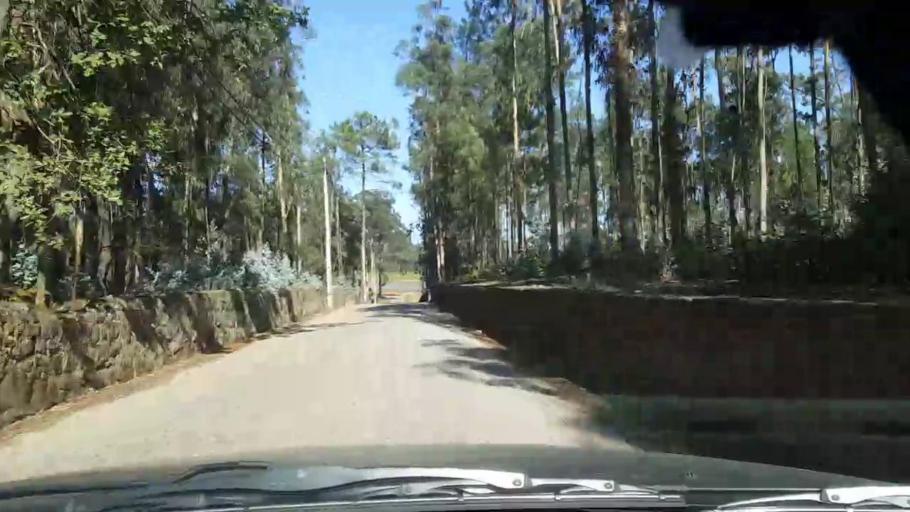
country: PT
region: Braga
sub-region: Vila Nova de Famalicao
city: Ribeirao
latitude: 41.3841
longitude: -8.6396
